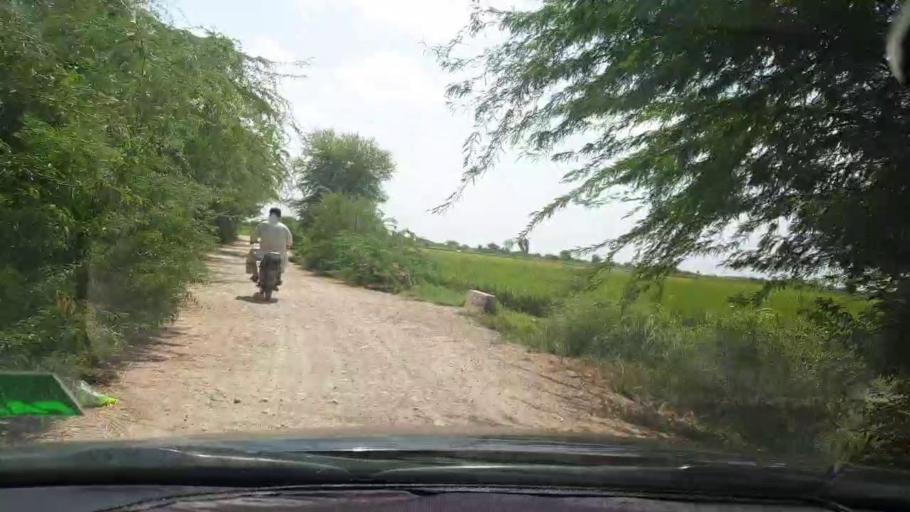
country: PK
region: Sindh
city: Tando Bago
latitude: 24.8793
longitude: 69.0803
